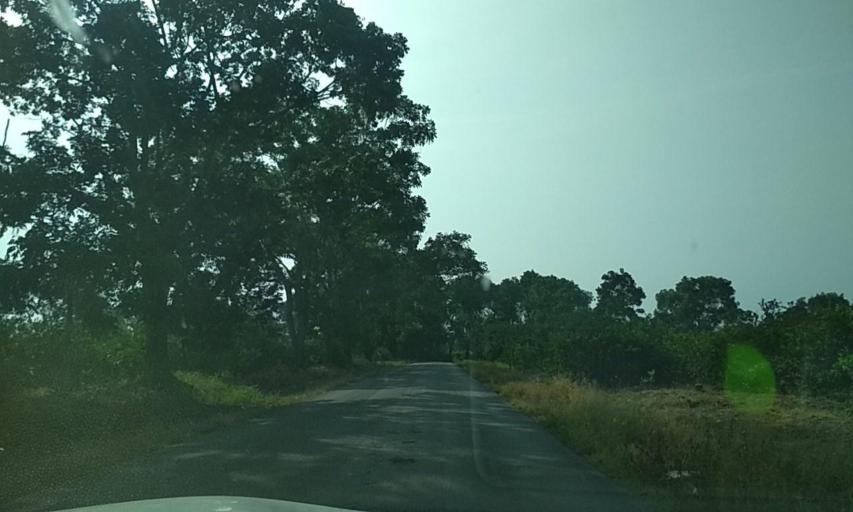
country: MX
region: Veracruz
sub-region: Martinez de la Torre
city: El Progreso
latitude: 20.1513
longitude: -97.0671
